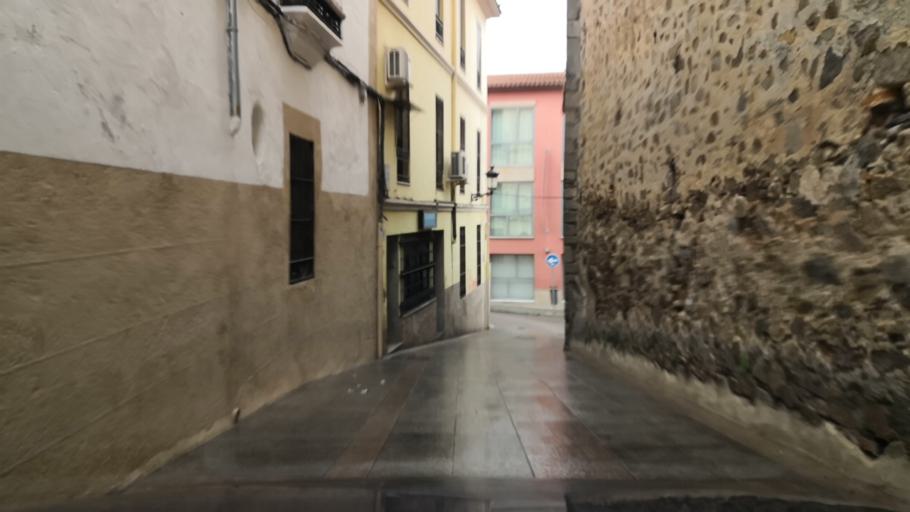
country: ES
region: Extremadura
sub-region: Provincia de Caceres
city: Caceres
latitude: 39.4765
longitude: -6.3722
